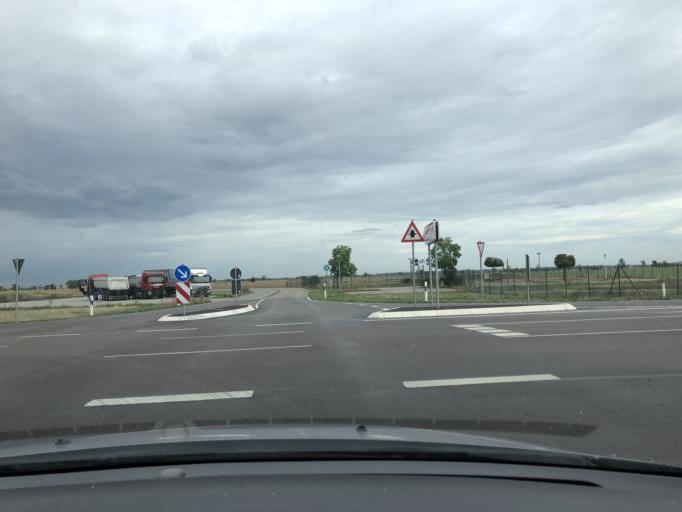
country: DE
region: Saxony-Anhalt
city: Gross Rosenburg
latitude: 51.8787
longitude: 11.8593
